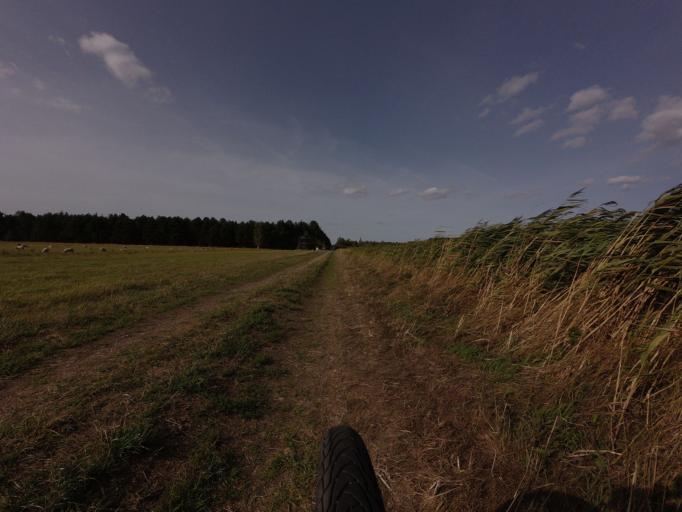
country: DK
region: Zealand
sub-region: Vordingborg Kommune
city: Praesto
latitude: 55.1387
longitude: 12.0895
